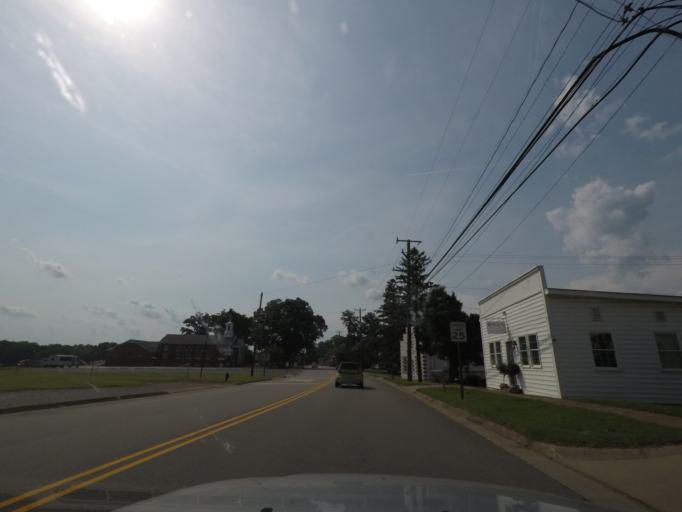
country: US
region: Virginia
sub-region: Buckingham County
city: Buckingham
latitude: 37.5430
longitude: -78.4588
